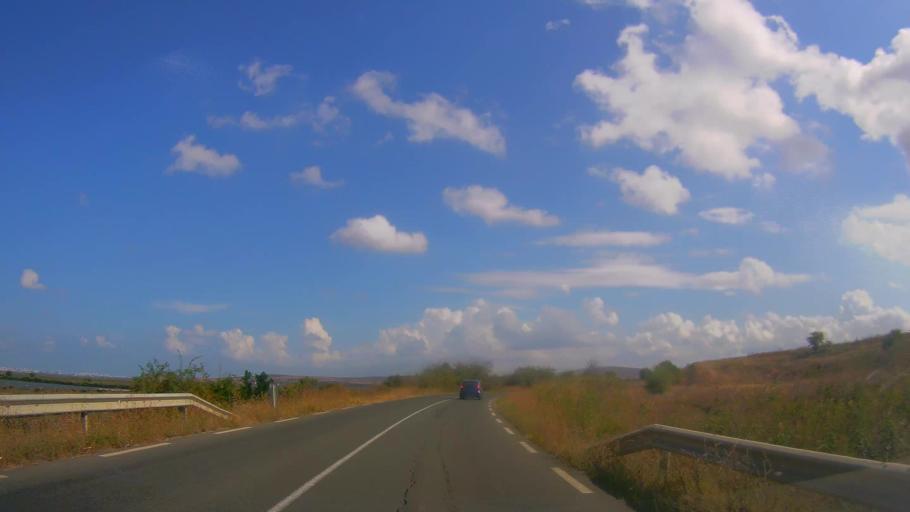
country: BG
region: Burgas
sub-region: Obshtina Kameno
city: Kameno
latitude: 42.4911
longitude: 27.3372
